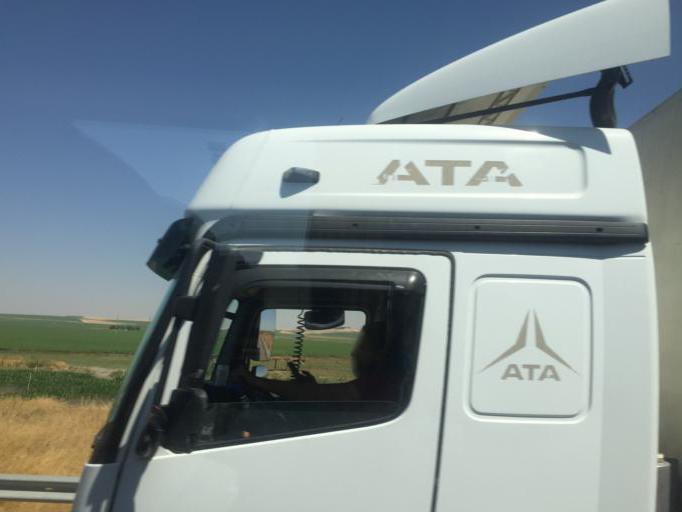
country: TR
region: Diyarbakir
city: Tepe
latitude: 37.8503
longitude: 40.7756
